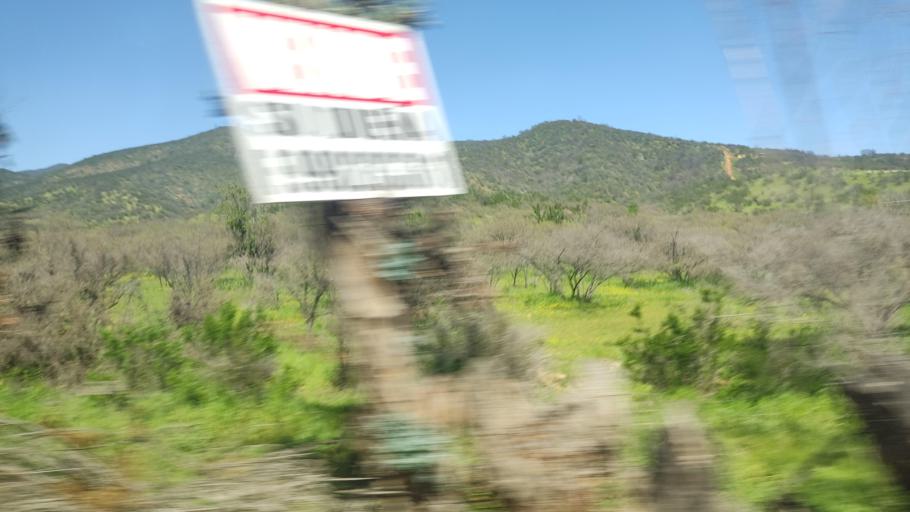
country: CL
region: Valparaiso
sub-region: Provincia de Marga Marga
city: Villa Alemana
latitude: -33.1628
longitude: -71.3211
